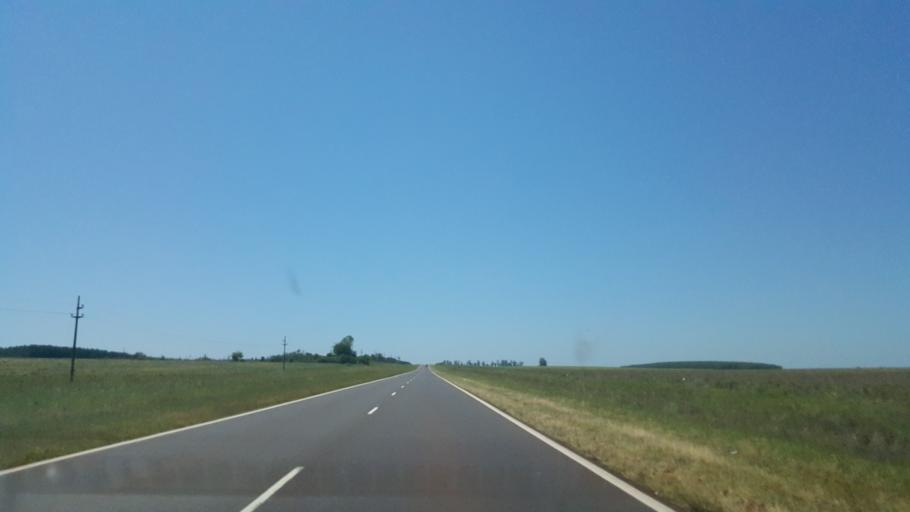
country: AR
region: Corrientes
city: Santo Tome
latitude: -28.4076
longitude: -56.1076
